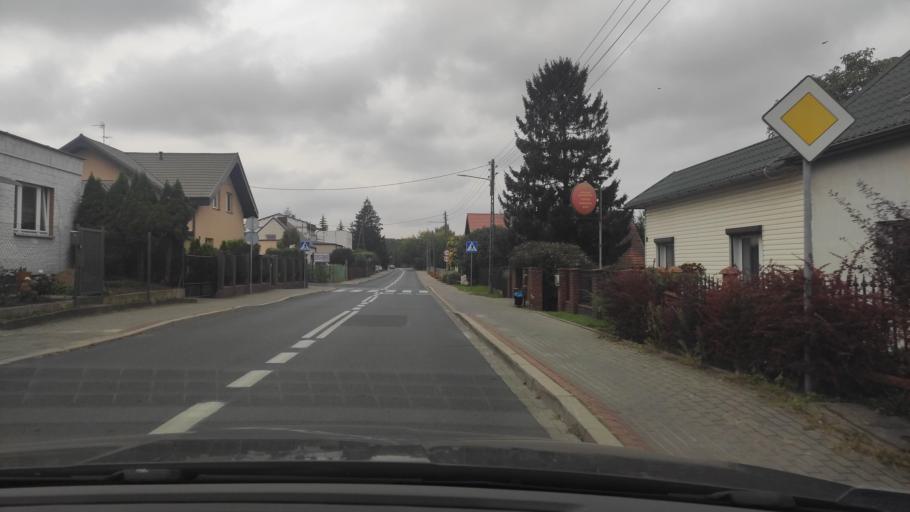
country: PL
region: Greater Poland Voivodeship
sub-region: Powiat poznanski
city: Swarzedz
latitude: 52.4088
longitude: 17.0545
